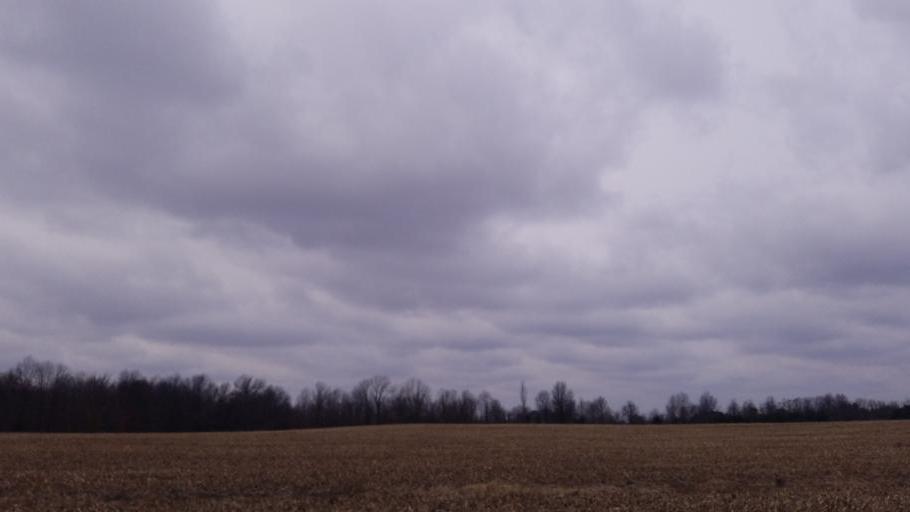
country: US
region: Ohio
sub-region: Crawford County
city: Galion
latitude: 40.6783
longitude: -82.7181
